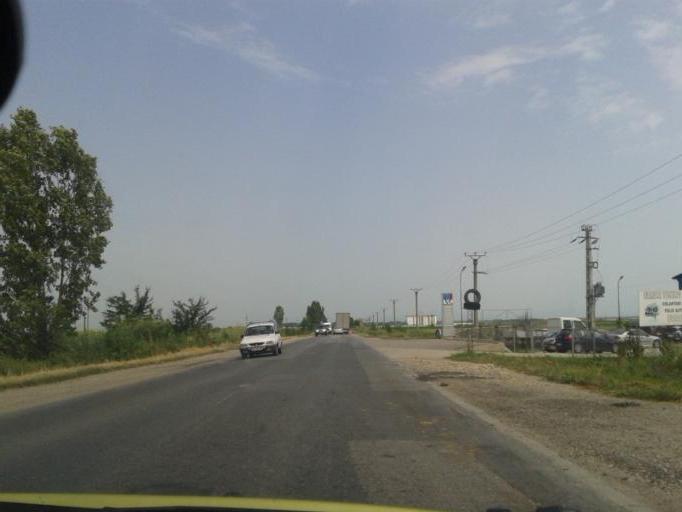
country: RO
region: Dambovita
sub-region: Oras Gaesti
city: Gaesti
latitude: 44.6865
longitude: 25.3137
